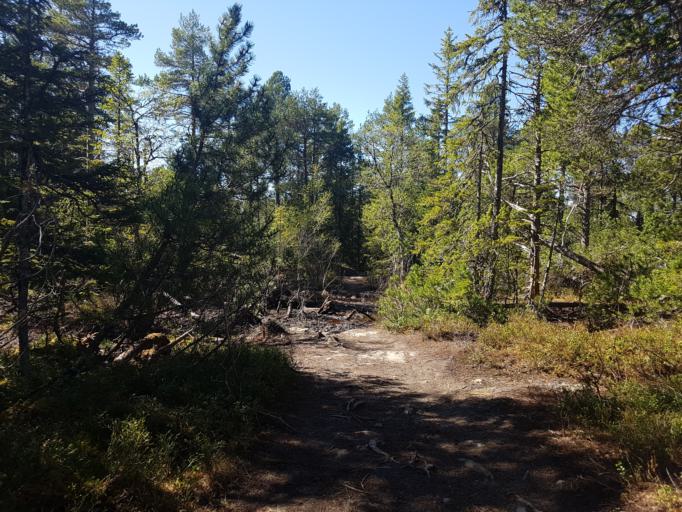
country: NO
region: Sor-Trondelag
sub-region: Trondheim
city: Trondheim
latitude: 63.4348
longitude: 10.3228
